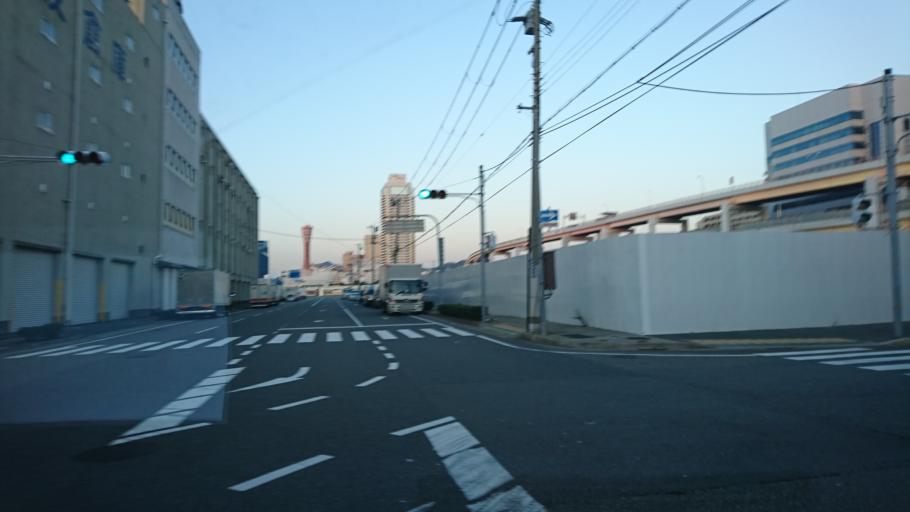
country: JP
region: Hyogo
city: Kobe
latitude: 34.6839
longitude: 135.1958
